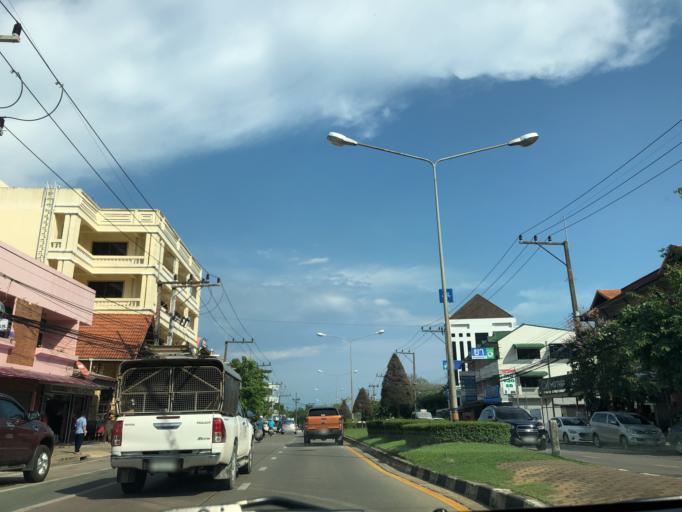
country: TH
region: Krabi
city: Krabi
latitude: 8.0761
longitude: 98.9159
